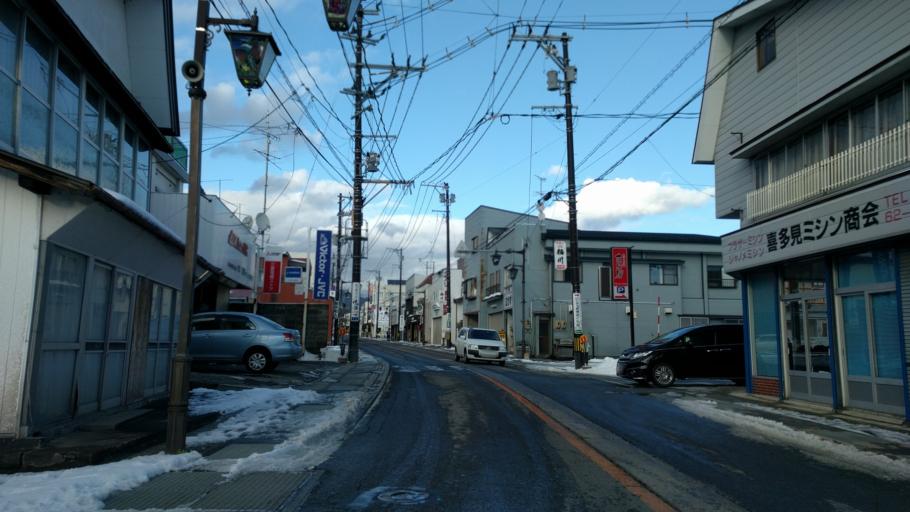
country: JP
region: Fukushima
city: Inawashiro
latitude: 37.5598
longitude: 140.1070
